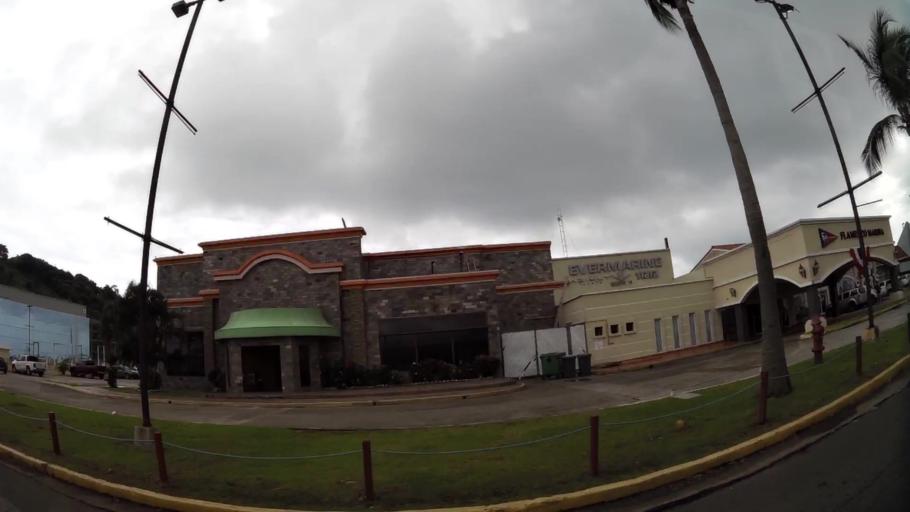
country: PA
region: Panama
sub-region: Distrito de Panama
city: Ancon
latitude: 8.9113
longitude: -79.5228
